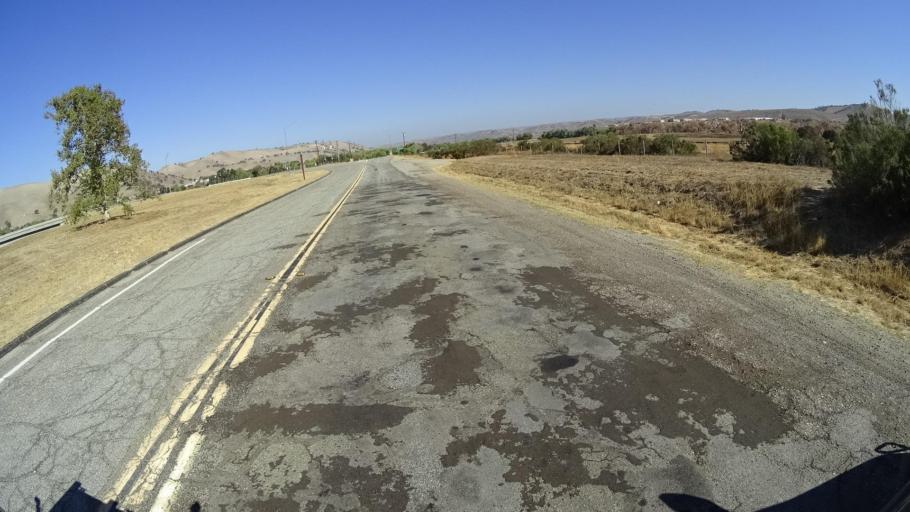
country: US
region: California
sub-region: San Luis Obispo County
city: San Miguel
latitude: 35.8151
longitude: -120.7531
